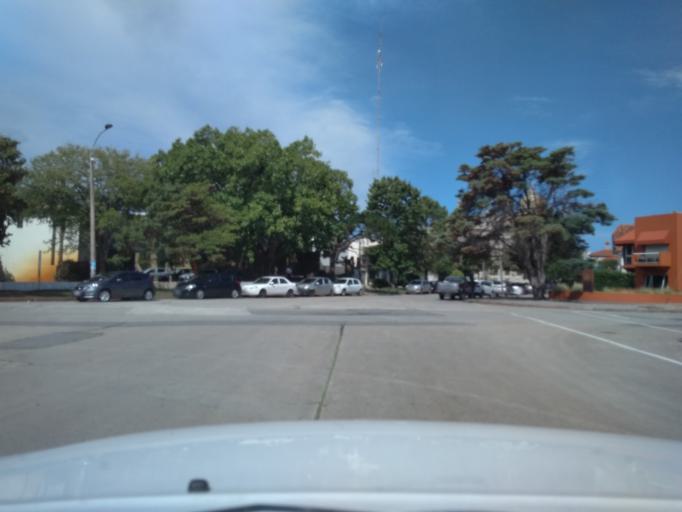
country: UY
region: Canelones
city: Paso de Carrasco
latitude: -34.8902
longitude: -56.0582
